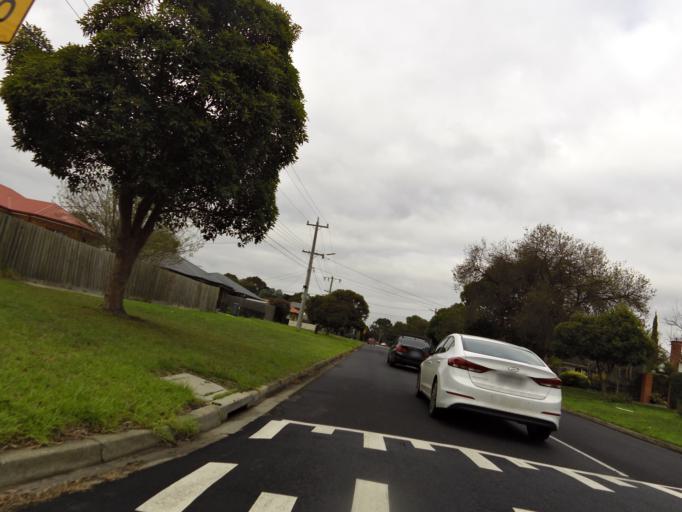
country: AU
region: Victoria
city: Heidelberg West
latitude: -37.7527
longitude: 145.0339
